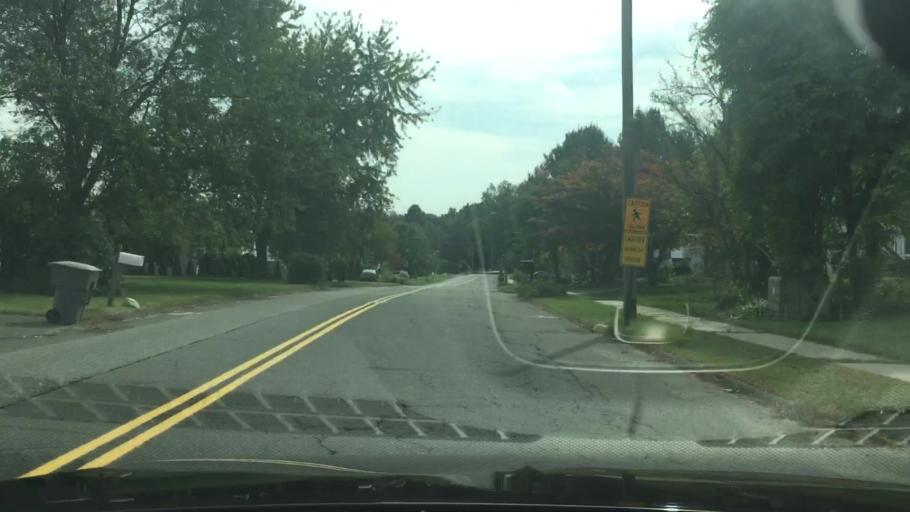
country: US
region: Connecticut
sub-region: Hartford County
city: Hazardville
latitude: 42.0076
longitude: -72.5112
